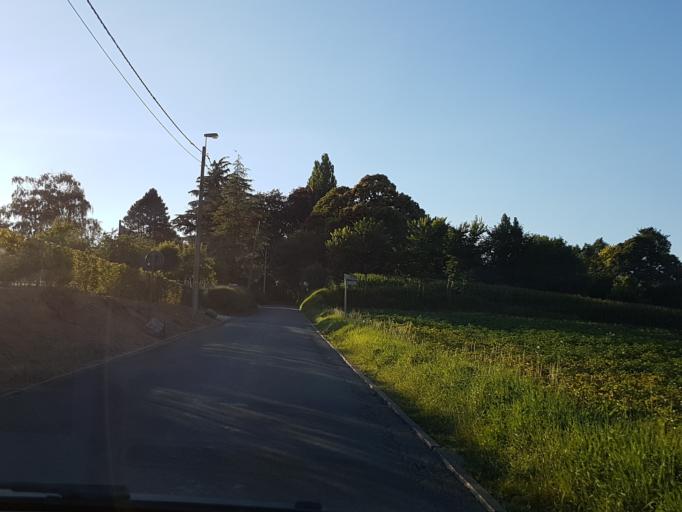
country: BE
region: Flanders
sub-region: Provincie Vlaams-Brabant
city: Asse
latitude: 50.8929
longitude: 4.2049
